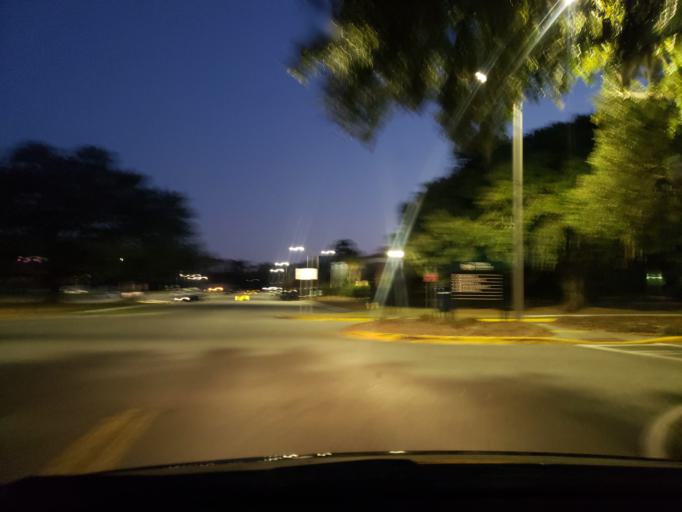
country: US
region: Georgia
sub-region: Chatham County
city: Montgomery
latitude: 31.9820
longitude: -81.1612
